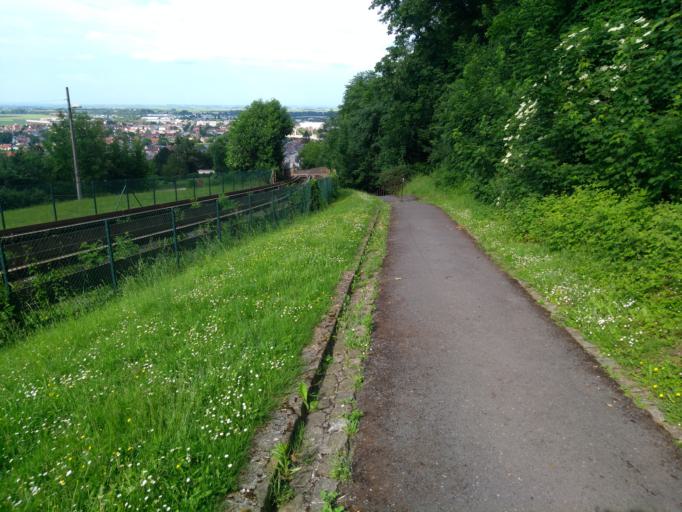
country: FR
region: Picardie
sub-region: Departement de l'Aisne
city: Laon
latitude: 49.5658
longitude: 3.6274
